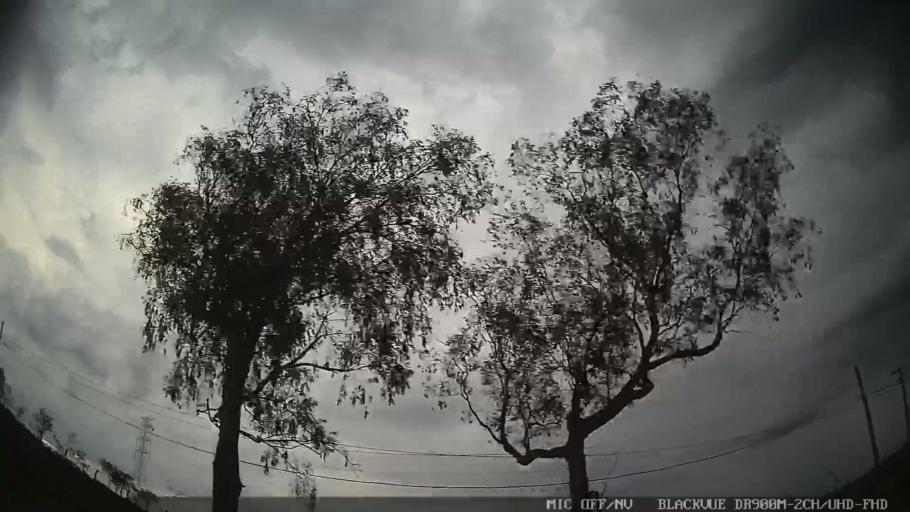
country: BR
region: Sao Paulo
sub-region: Amparo
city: Amparo
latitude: -22.7452
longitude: -46.7631
